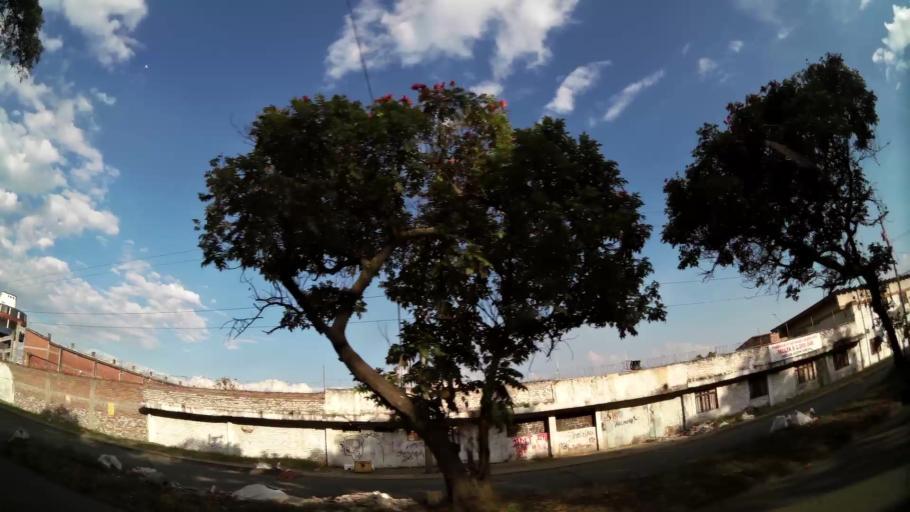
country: CO
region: Valle del Cauca
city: Cali
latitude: 3.4324
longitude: -76.4965
